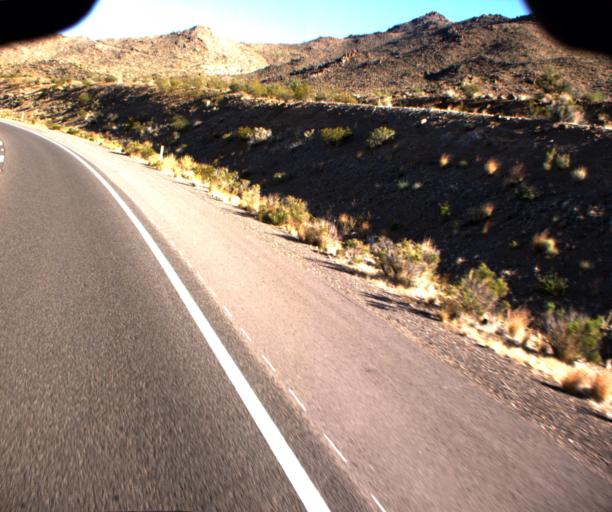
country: US
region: Arizona
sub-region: Mohave County
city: Kingman
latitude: 35.2210
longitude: -114.1214
